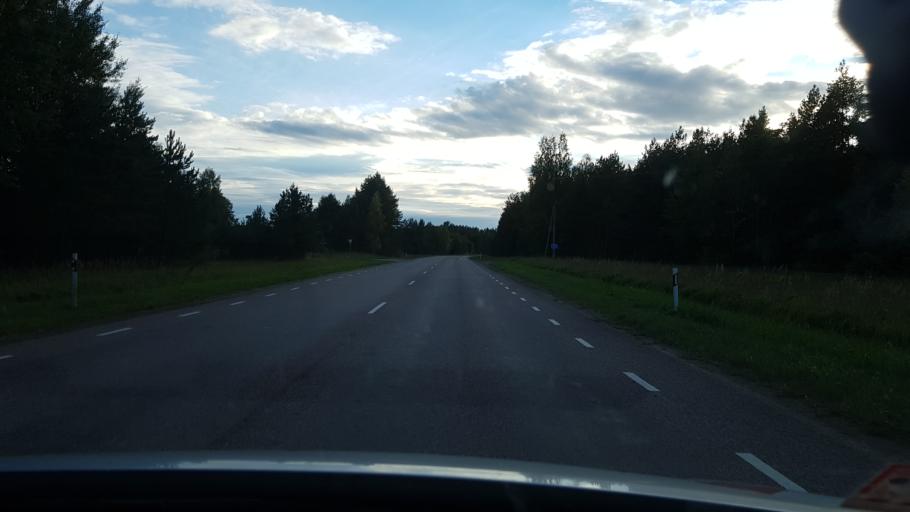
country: EE
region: Vorumaa
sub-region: Voru linn
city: Voru
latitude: 57.7927
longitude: 26.9459
